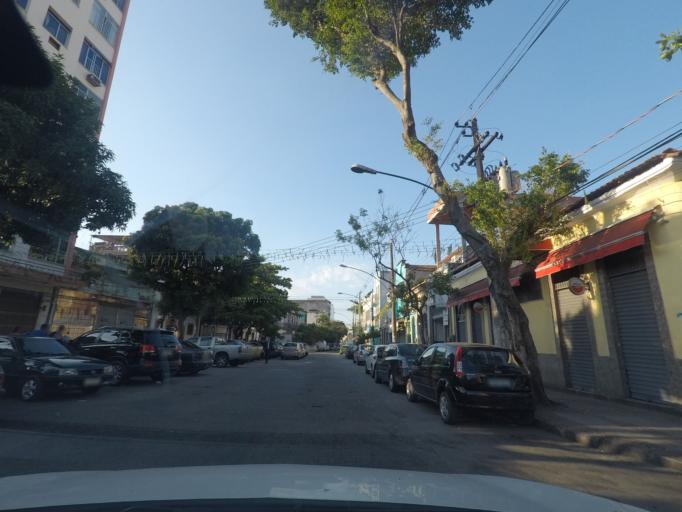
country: BR
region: Rio de Janeiro
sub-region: Rio De Janeiro
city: Rio de Janeiro
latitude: -22.9156
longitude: -43.1957
